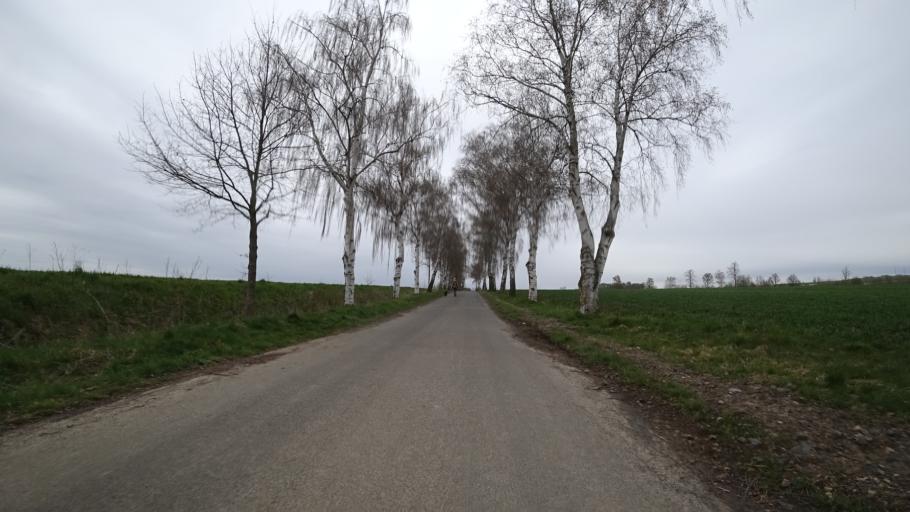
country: DE
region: Hesse
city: Grebenstein
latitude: 51.4279
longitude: 9.4297
